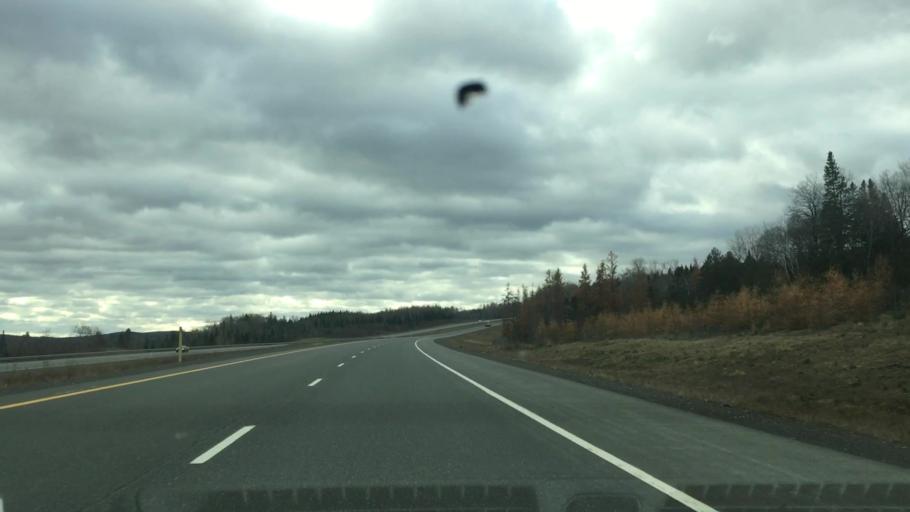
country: US
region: Maine
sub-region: Aroostook County
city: Fort Fairfield
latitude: 46.6712
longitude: -67.7298
